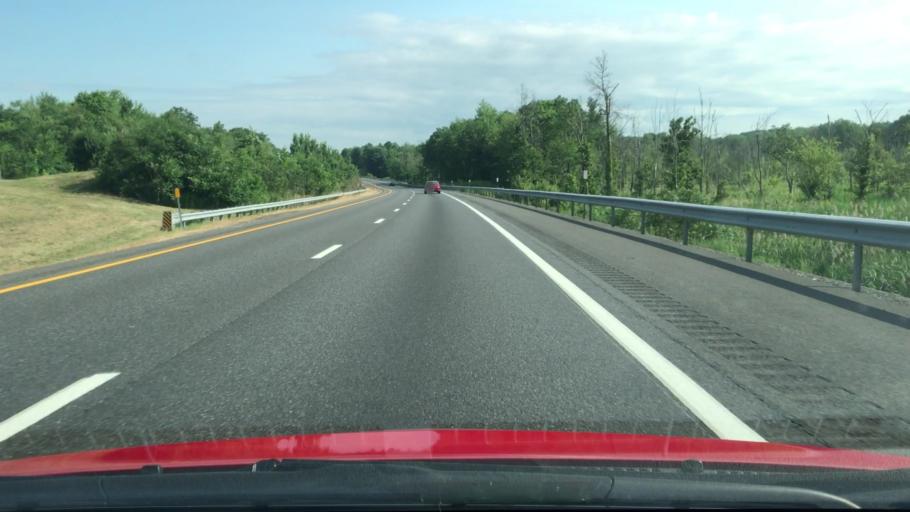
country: US
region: New York
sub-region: Ulster County
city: Plattekill
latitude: 41.6458
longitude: -74.0765
